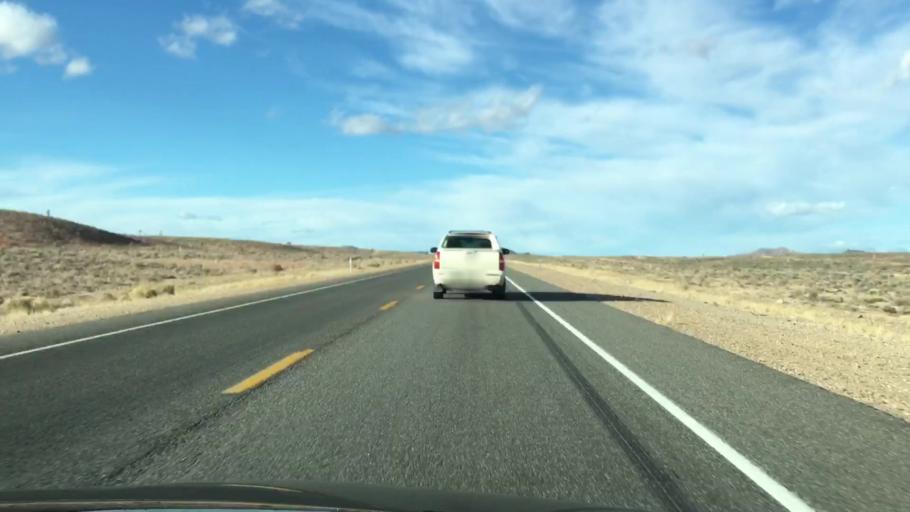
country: US
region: Nevada
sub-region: Esmeralda County
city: Goldfield
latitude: 37.5616
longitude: -117.1990
